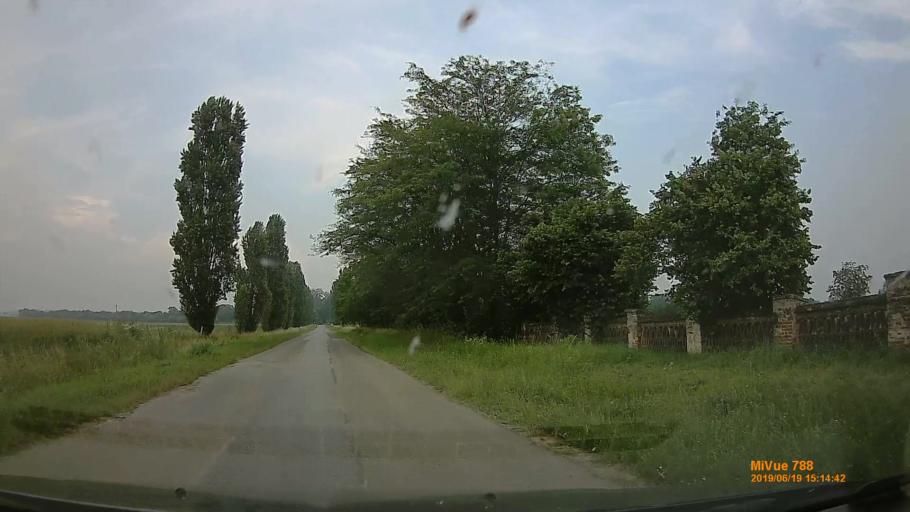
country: HU
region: Baranya
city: Szigetvar
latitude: 46.0699
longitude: 17.8273
